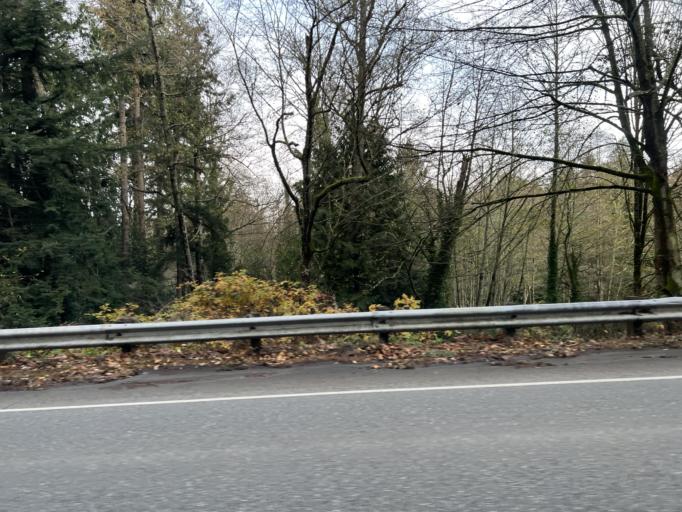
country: US
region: Washington
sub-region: Kitsap County
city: Bainbridge Island
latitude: 47.6479
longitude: -122.5204
